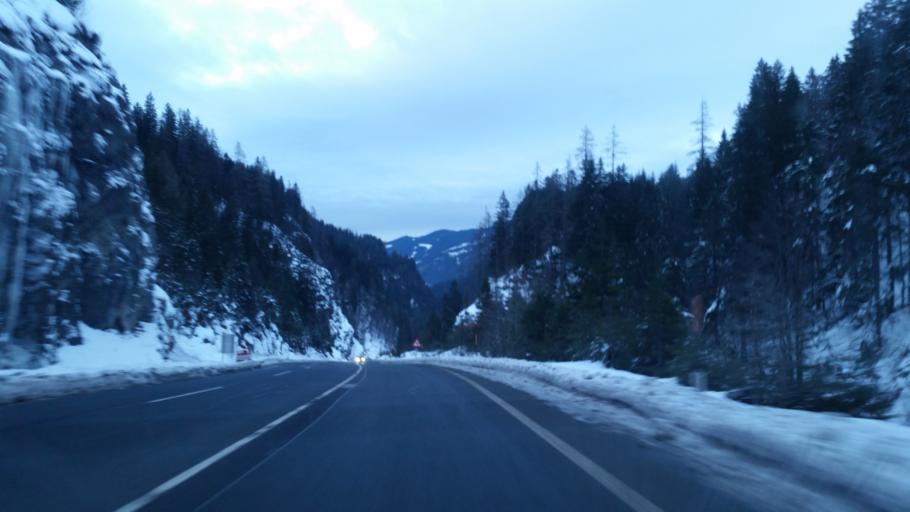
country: AT
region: Salzburg
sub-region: Politischer Bezirk Sankt Johann im Pongau
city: Untertauern
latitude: 47.2707
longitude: 13.5002
